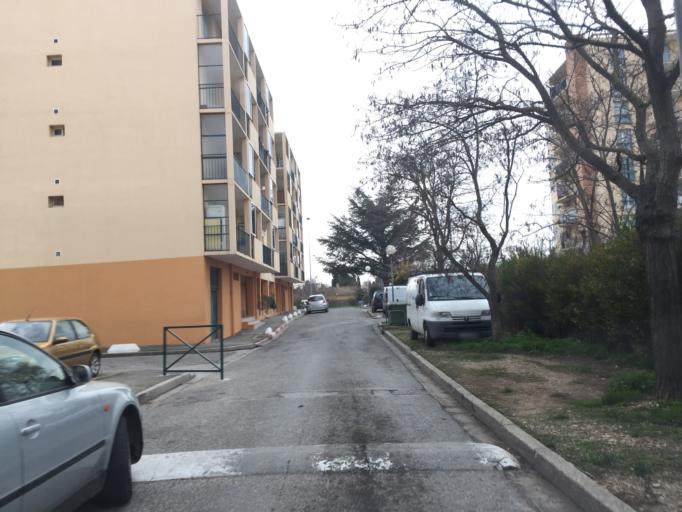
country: FR
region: Provence-Alpes-Cote d'Azur
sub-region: Departement du Vaucluse
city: Sorgues
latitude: 44.0142
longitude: 4.8604
